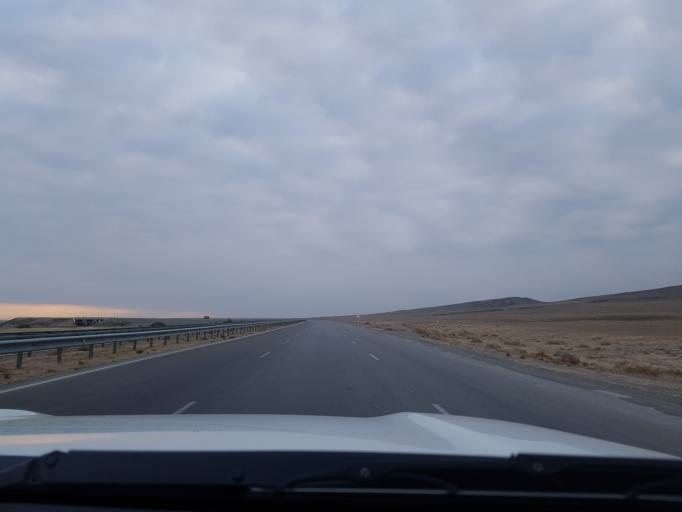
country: IR
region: Razavi Khorasan
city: Dargaz
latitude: 37.6840
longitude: 59.0705
